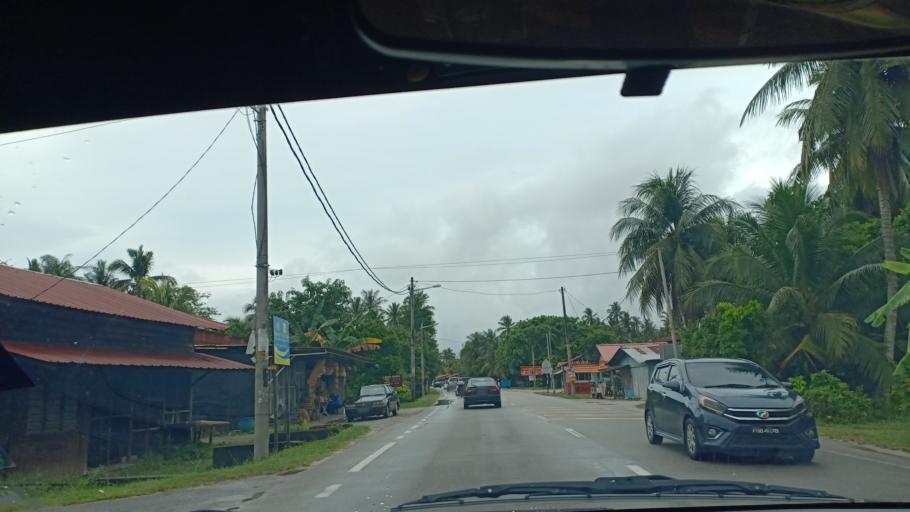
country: MY
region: Penang
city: Kepala Batas
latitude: 5.4973
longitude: 100.4426
